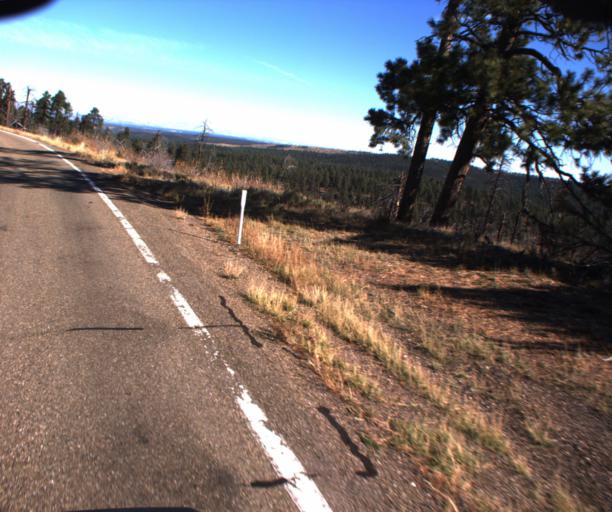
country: US
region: Arizona
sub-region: Coconino County
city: Fredonia
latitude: 36.7719
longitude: -112.2526
